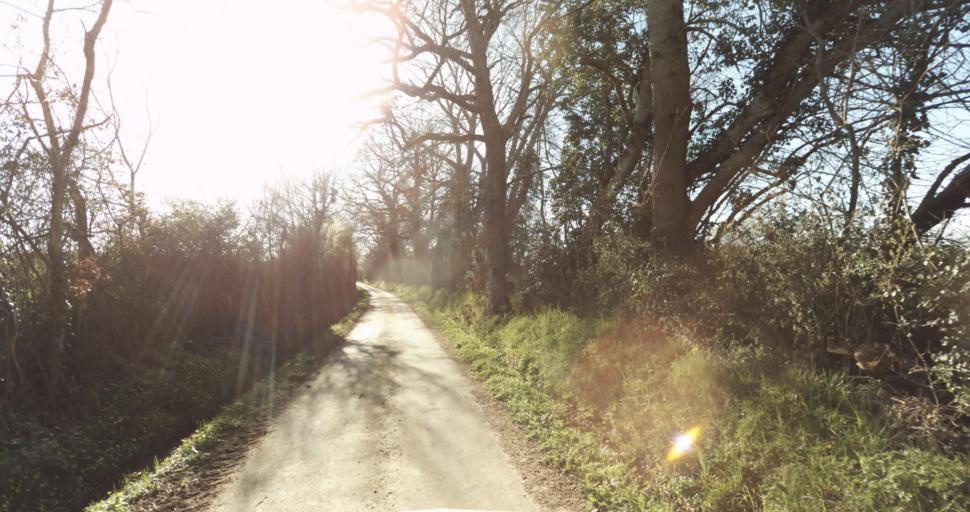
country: FR
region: Lower Normandy
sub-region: Departement du Calvados
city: Saint-Pierre-sur-Dives
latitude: 49.0476
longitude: 0.0516
